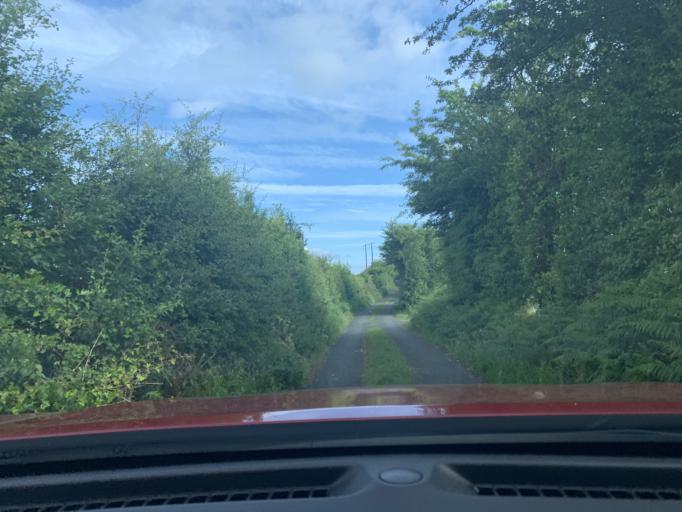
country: IE
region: Connaught
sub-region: Sligo
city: Sligo
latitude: 54.2308
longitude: -8.4659
